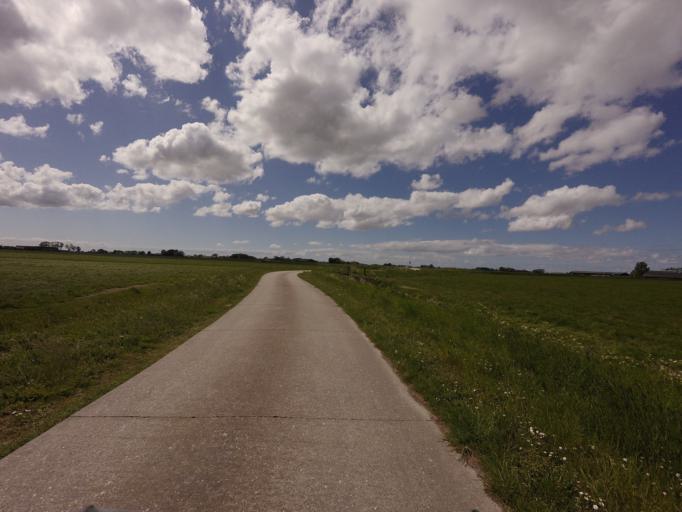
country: NL
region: Friesland
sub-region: Gemeente Franekeradeel
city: Tzum
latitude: 53.1292
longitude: 5.5583
